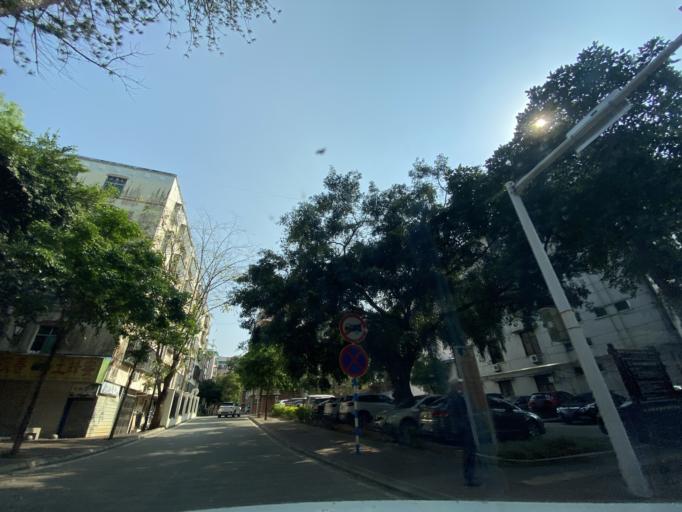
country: CN
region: Hainan
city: Chongshan
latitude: 18.7771
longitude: 109.5140
